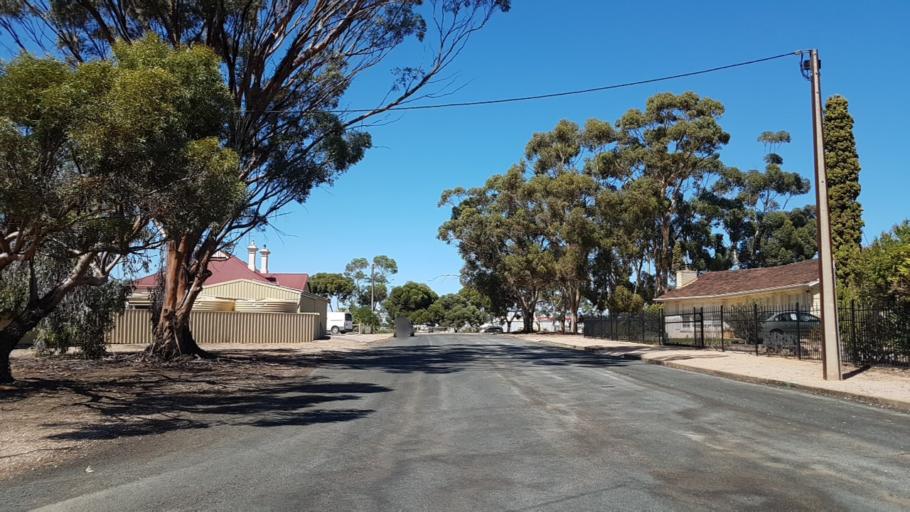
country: AU
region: South Australia
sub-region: Copper Coast
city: Kadina
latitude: -33.9651
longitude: 137.7191
